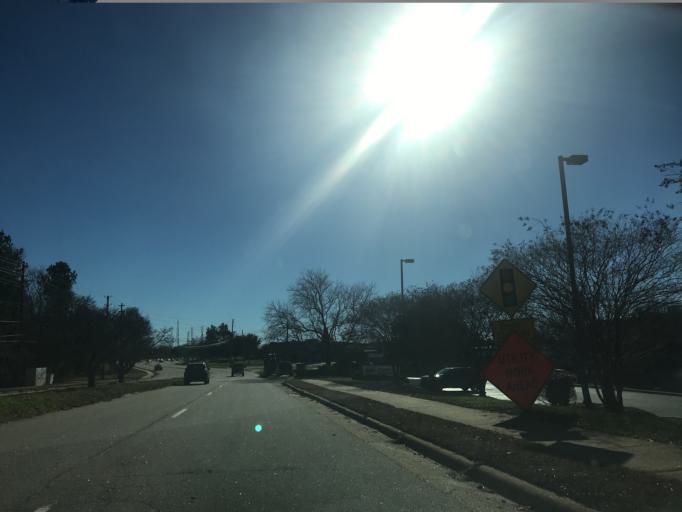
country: US
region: North Carolina
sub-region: Wake County
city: West Raleigh
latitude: 35.8127
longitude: -78.7058
